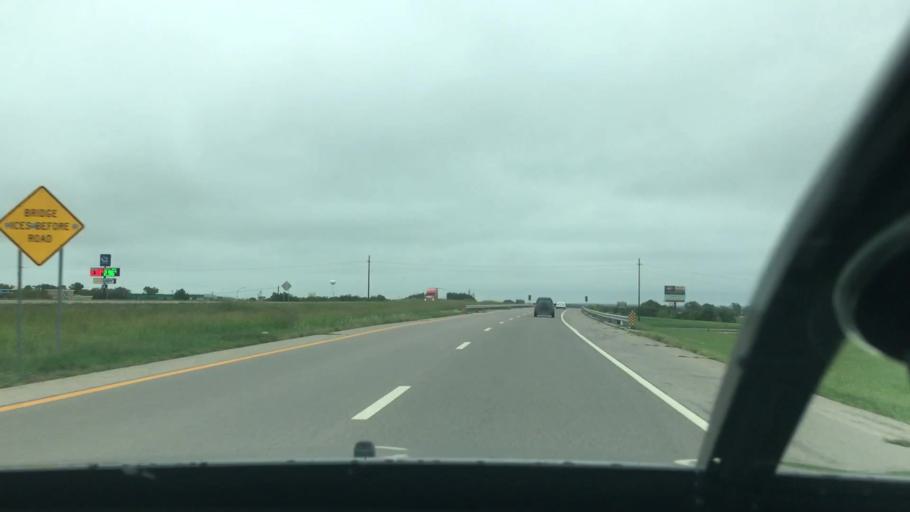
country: US
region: Oklahoma
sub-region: Okfuskee County
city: Okemah
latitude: 35.4220
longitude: -96.3024
